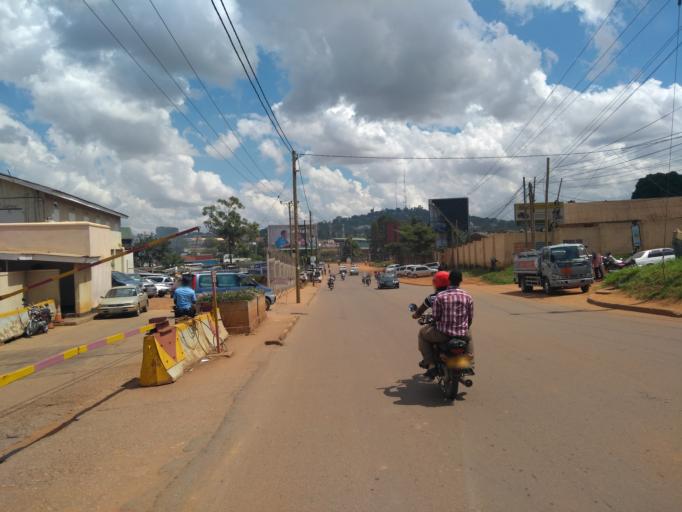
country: UG
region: Central Region
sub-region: Kampala District
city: Kampala
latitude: 0.3213
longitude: 32.6113
